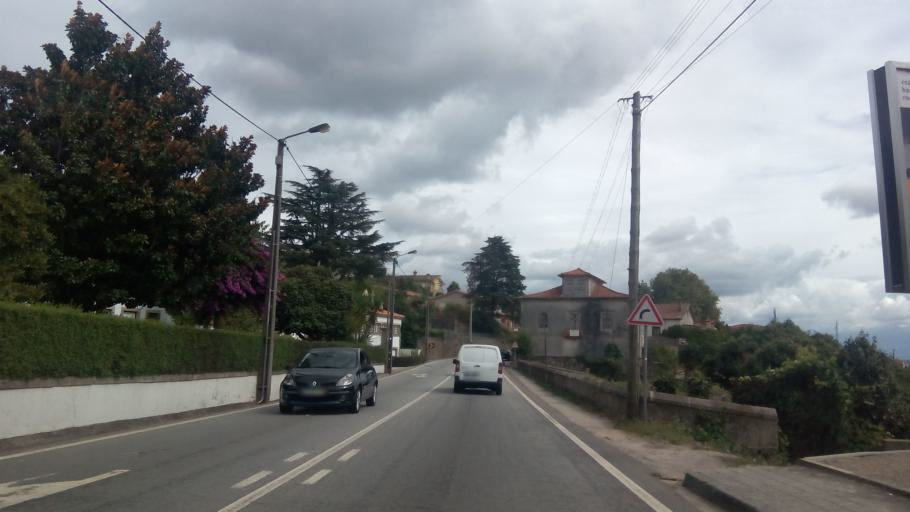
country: PT
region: Porto
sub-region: Paredes
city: Baltar
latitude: 41.1911
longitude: -8.4028
